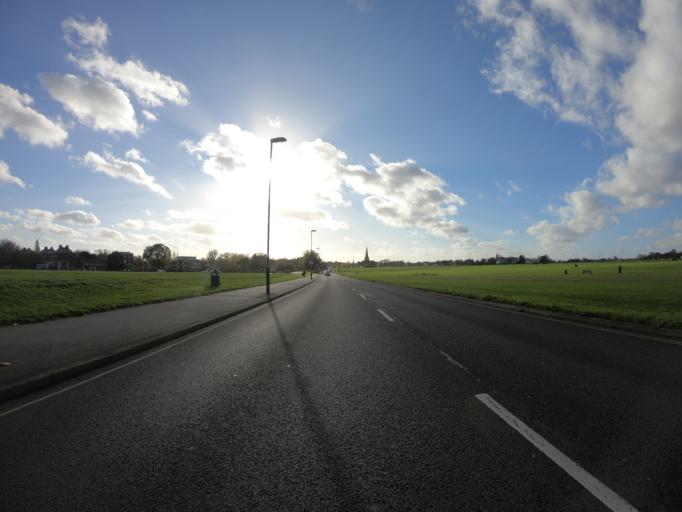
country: GB
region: England
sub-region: Greater London
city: Blackheath
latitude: 51.4715
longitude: 0.0128
